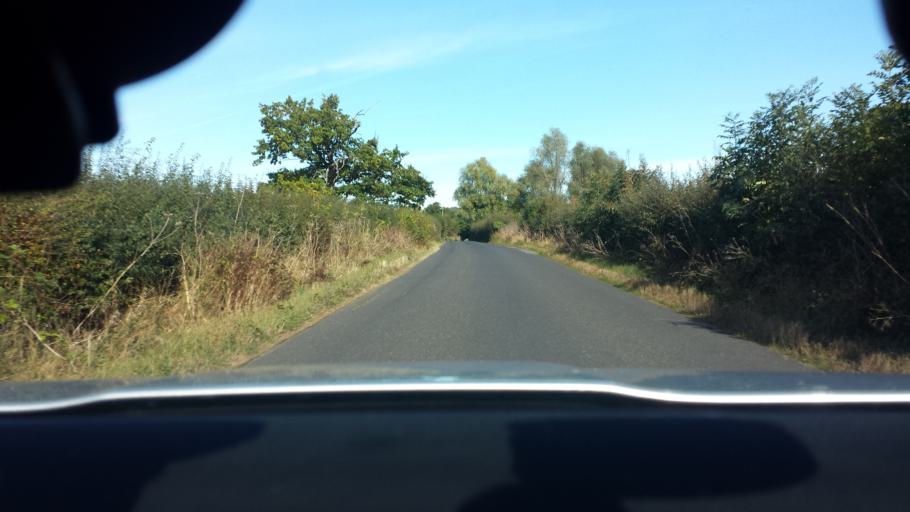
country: GB
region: England
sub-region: Kent
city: Staplehurst
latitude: 51.2009
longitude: 0.5549
